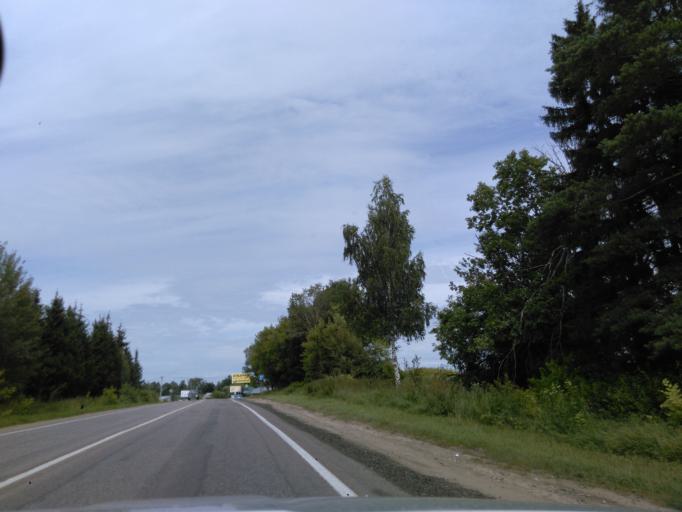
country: RU
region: Moskovskaya
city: Solnechnogorsk
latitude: 56.1436
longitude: 36.9169
